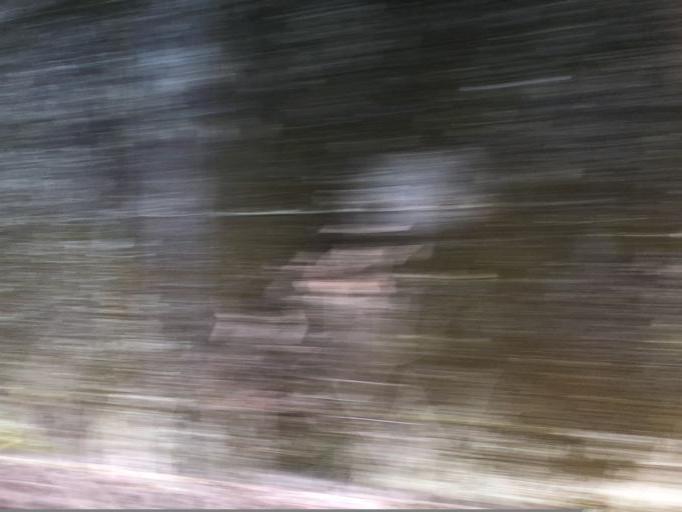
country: JP
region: Kochi
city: Nakamura
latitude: 33.0396
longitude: 133.0337
